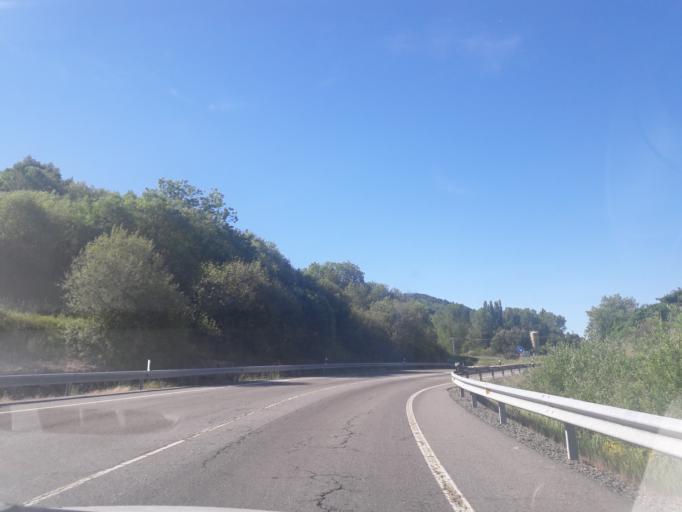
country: ES
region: Castille and Leon
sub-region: Provincia de Salamanca
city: Puerto de Bejar
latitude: 40.3475
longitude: -5.8444
